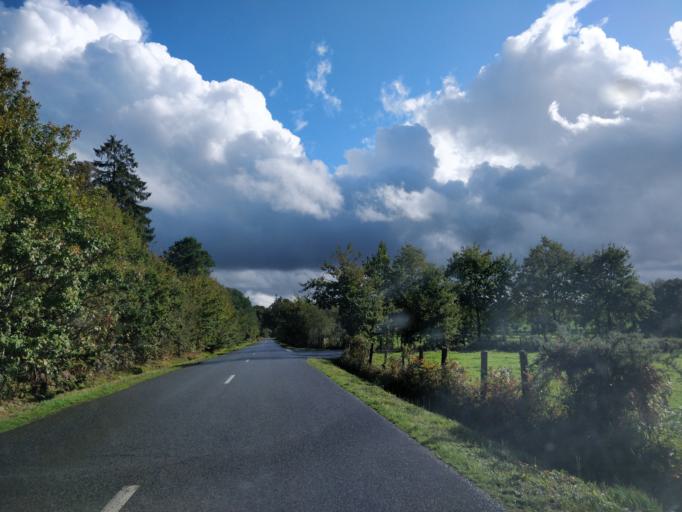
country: FR
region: Brittany
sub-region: Departement d'Ille-et-Vilaine
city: Chateaubourg
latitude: 48.1454
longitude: -1.4030
